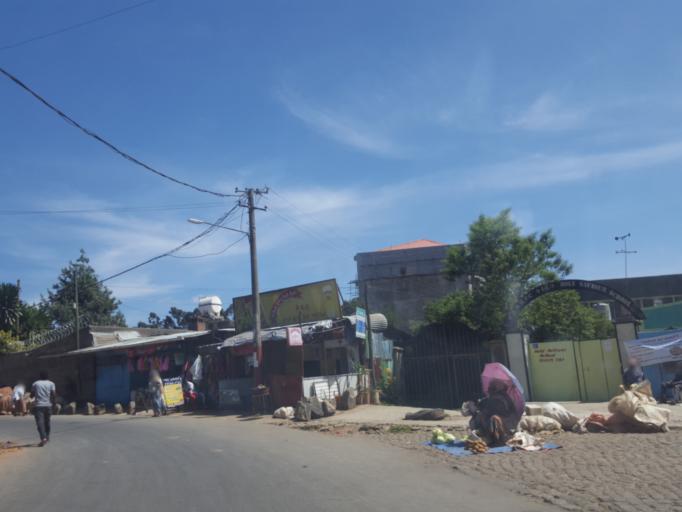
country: ET
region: Adis Abeba
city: Addis Ababa
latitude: 9.0588
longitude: 38.7290
